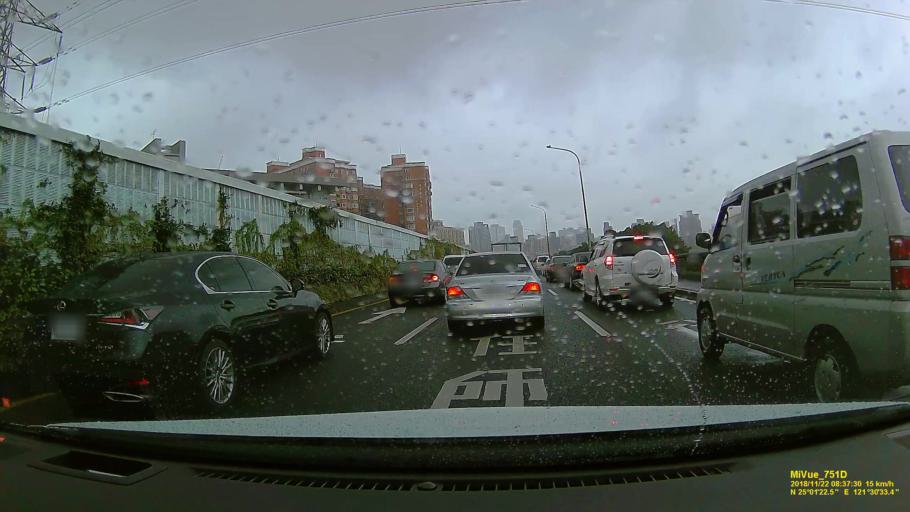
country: TW
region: Taipei
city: Taipei
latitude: 25.0230
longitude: 121.5095
